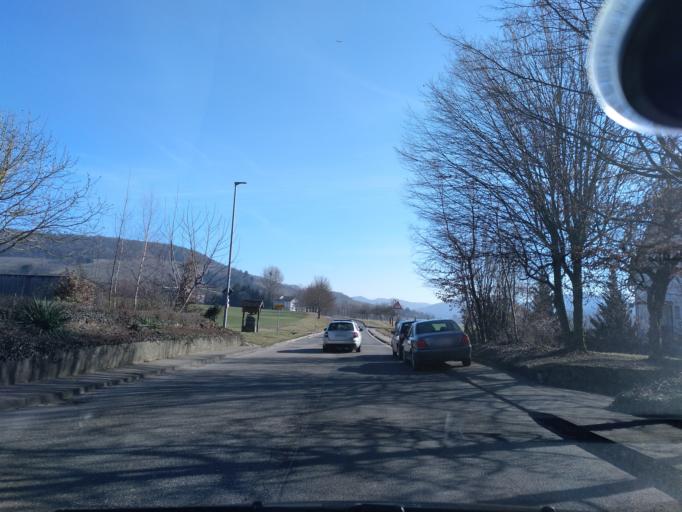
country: DE
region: Baden-Wuerttemberg
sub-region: Regierungsbezirk Stuttgart
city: Bretzfeld
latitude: 49.1628
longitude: 9.4528
